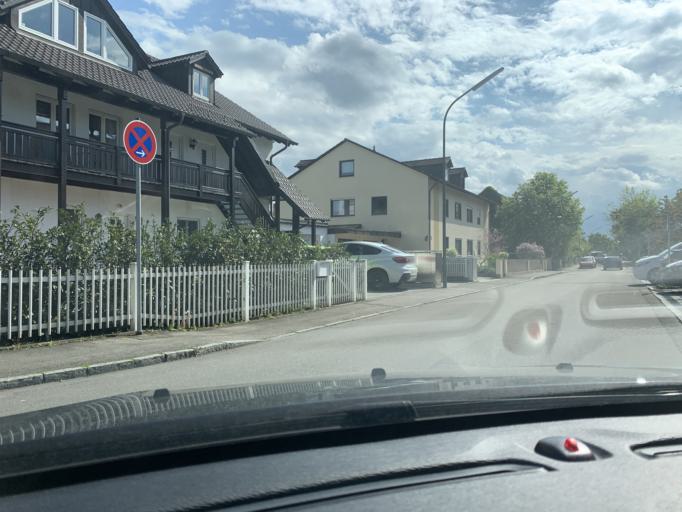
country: DE
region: Bavaria
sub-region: Upper Bavaria
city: Unterschleissheim
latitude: 48.2765
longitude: 11.5831
